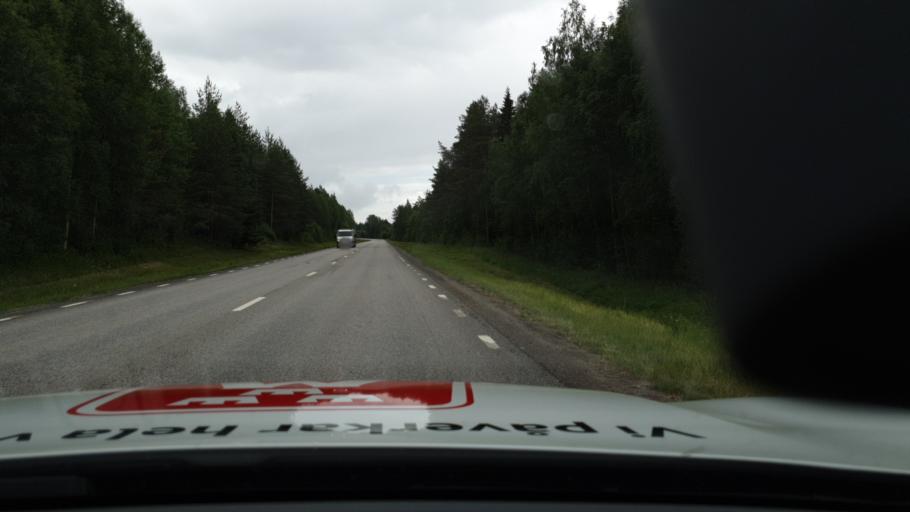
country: SE
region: Norrbotten
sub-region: Pitea Kommun
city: Rosvik
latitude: 65.5618
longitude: 21.7926
